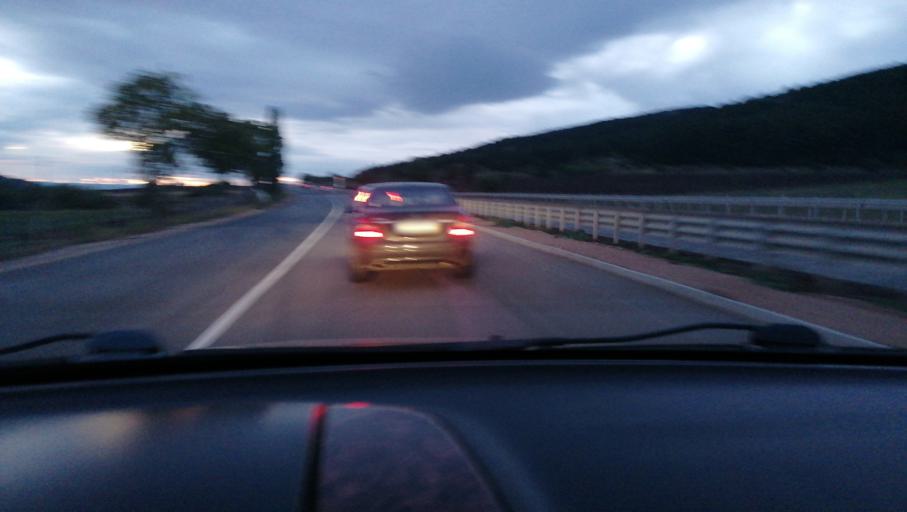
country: BG
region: Sofiya
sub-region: Obshtina Slivnitsa
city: Slivnitsa
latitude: 42.8507
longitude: 23.0722
